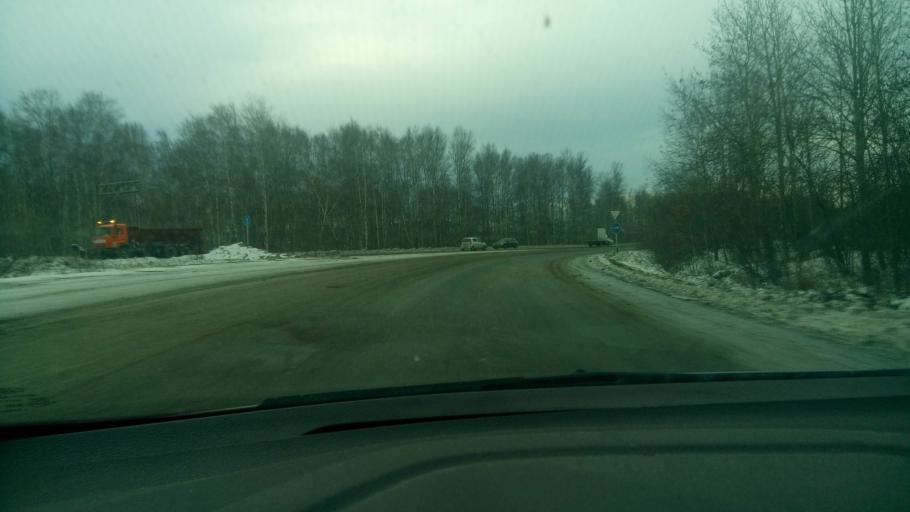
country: RU
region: Sverdlovsk
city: Istok
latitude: 56.7589
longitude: 60.7647
